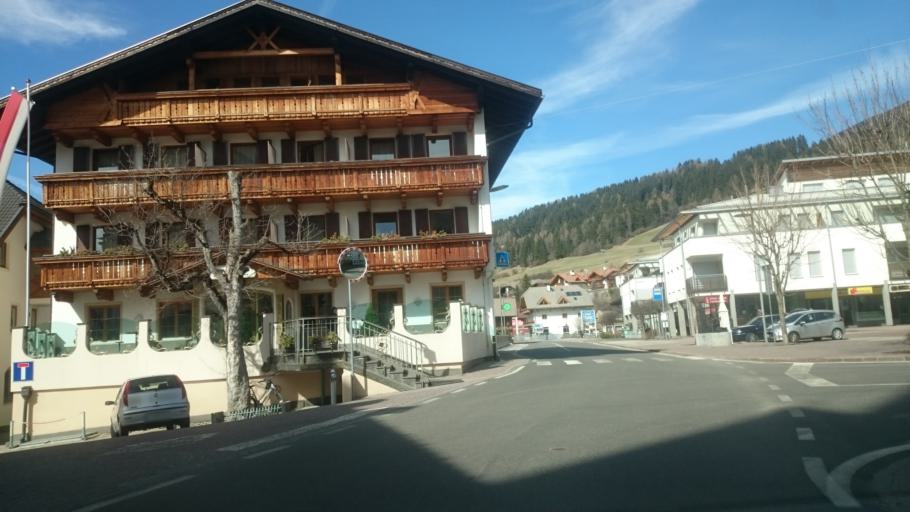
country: IT
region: Trentino-Alto Adige
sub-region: Bolzano
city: Monguelfo
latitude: 46.7571
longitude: 12.1043
